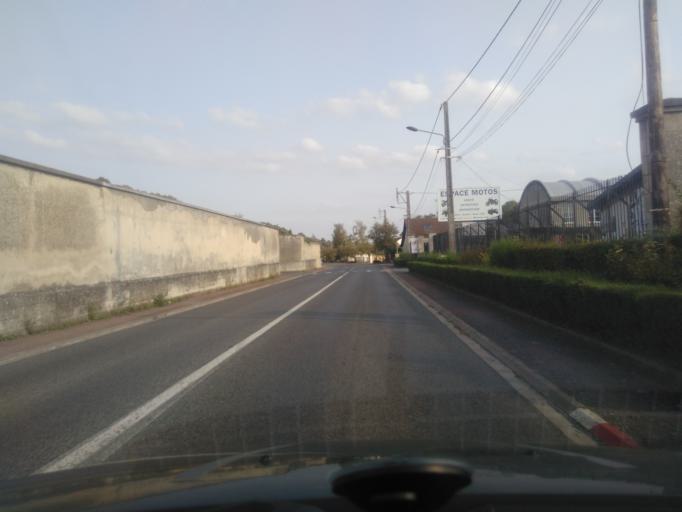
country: FR
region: Picardie
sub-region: Departement de l'Aisne
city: Laon
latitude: 49.5563
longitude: 3.6036
